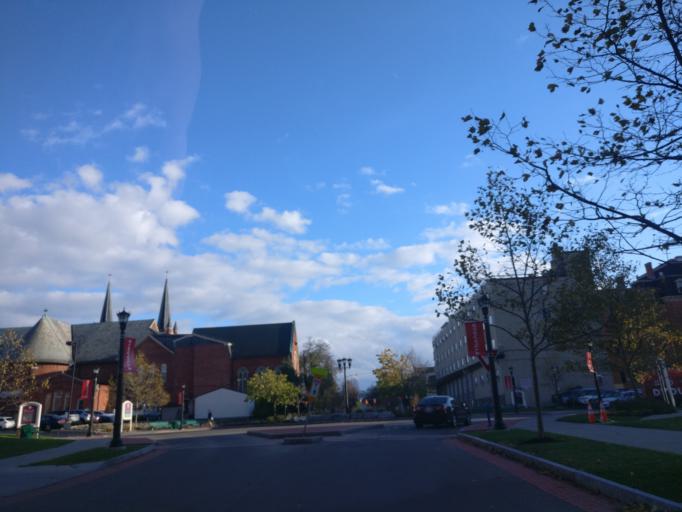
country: US
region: New York
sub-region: Erie County
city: Buffalo
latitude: 42.9037
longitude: -78.8909
